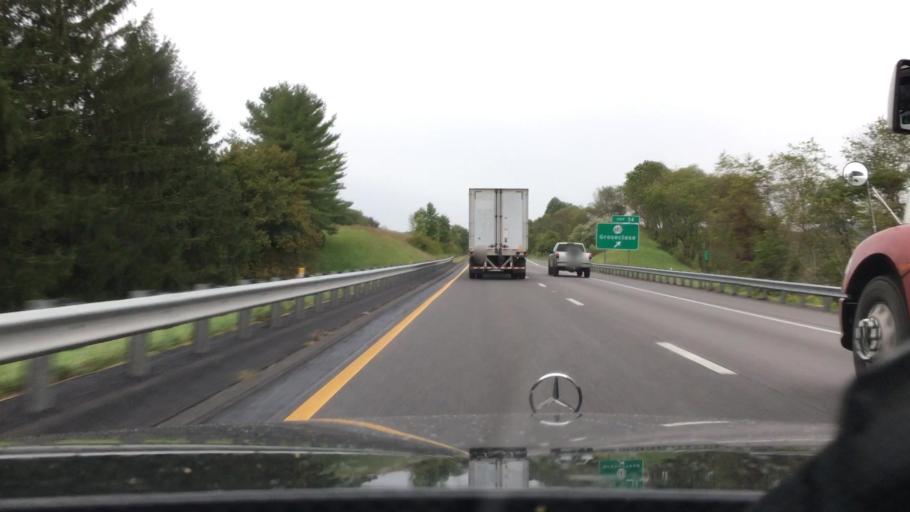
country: US
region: Virginia
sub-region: Smyth County
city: Atkins
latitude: 36.8928
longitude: -81.3613
